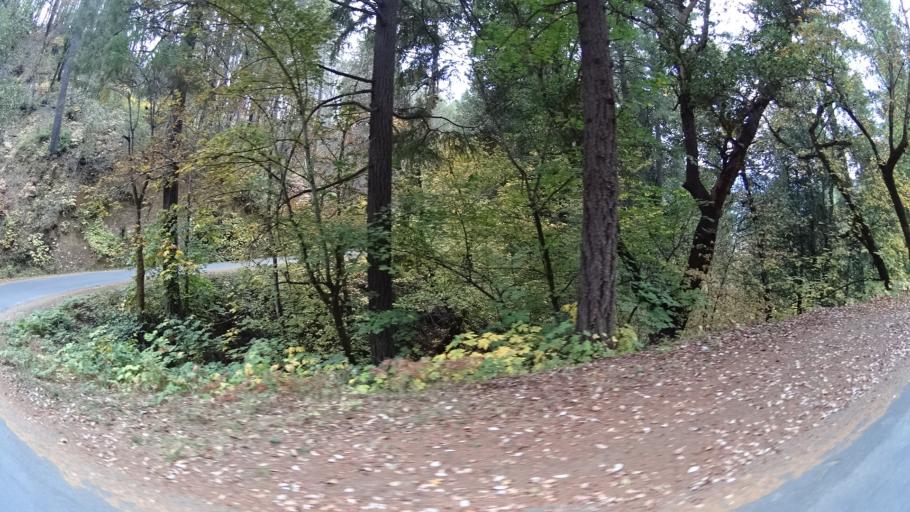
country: US
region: California
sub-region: Siskiyou County
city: Happy Camp
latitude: 41.7958
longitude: -123.3615
